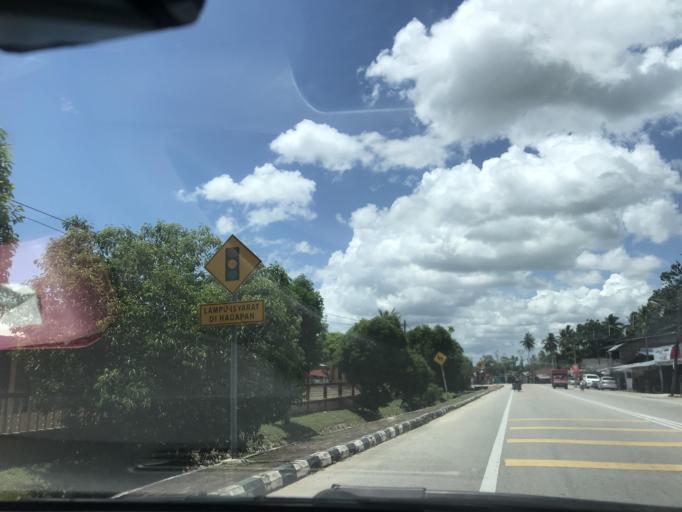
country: MY
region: Kelantan
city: Tumpat
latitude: 6.1888
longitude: 102.1588
